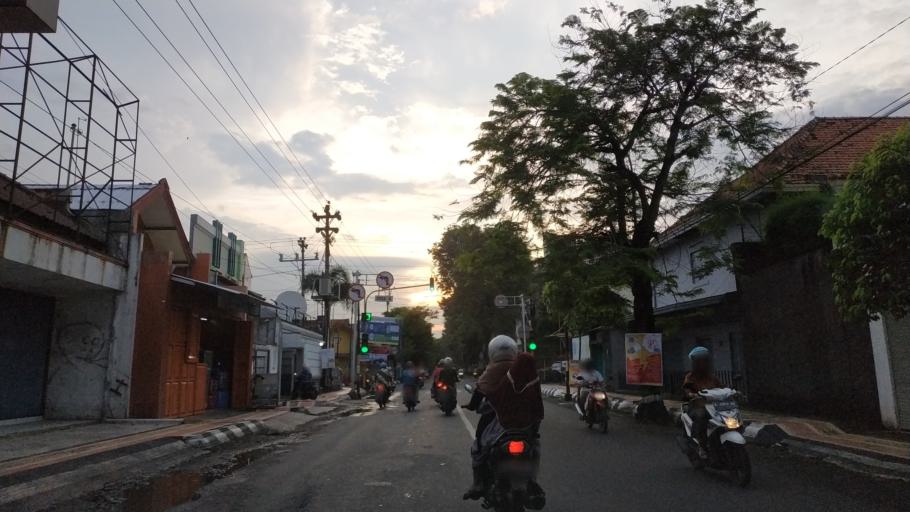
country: ID
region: Central Java
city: Kudus
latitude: -6.8106
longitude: 110.8479
